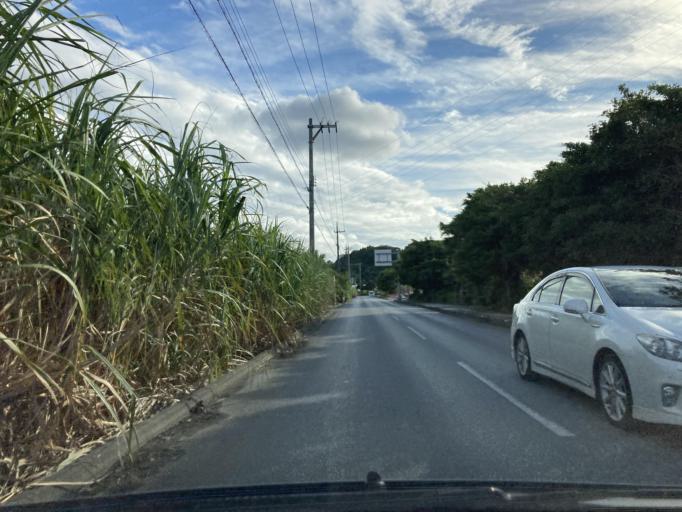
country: JP
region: Okinawa
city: Itoman
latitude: 26.1385
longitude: 127.7468
